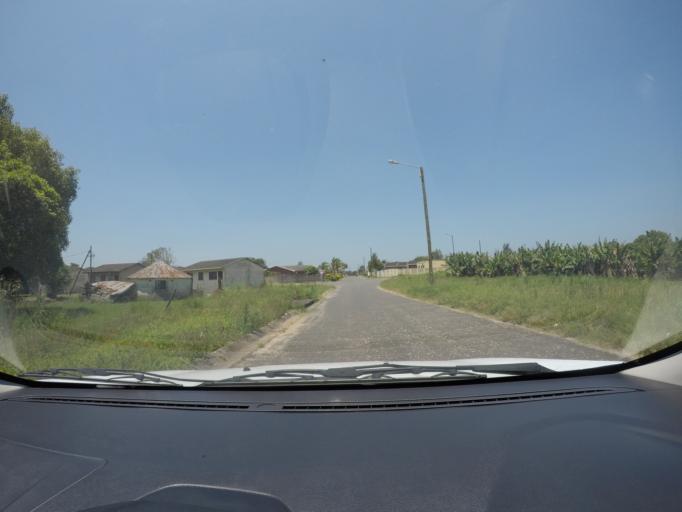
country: ZA
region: KwaZulu-Natal
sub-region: uThungulu District Municipality
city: eSikhawini
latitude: -28.8921
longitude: 31.8846
